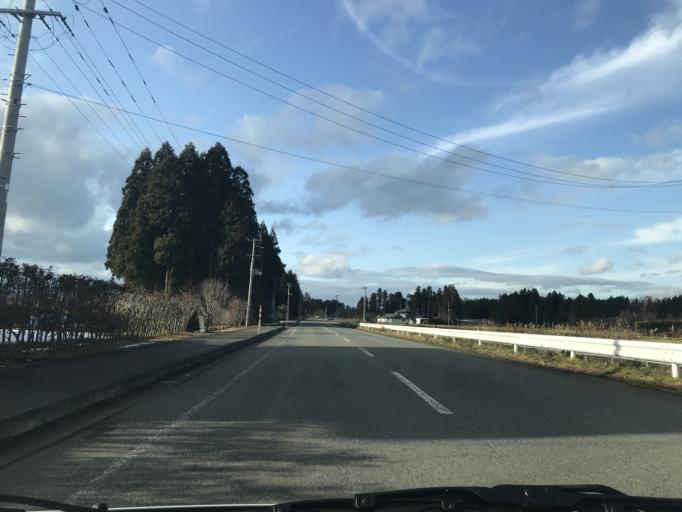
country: JP
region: Iwate
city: Mizusawa
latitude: 39.1903
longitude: 141.0751
